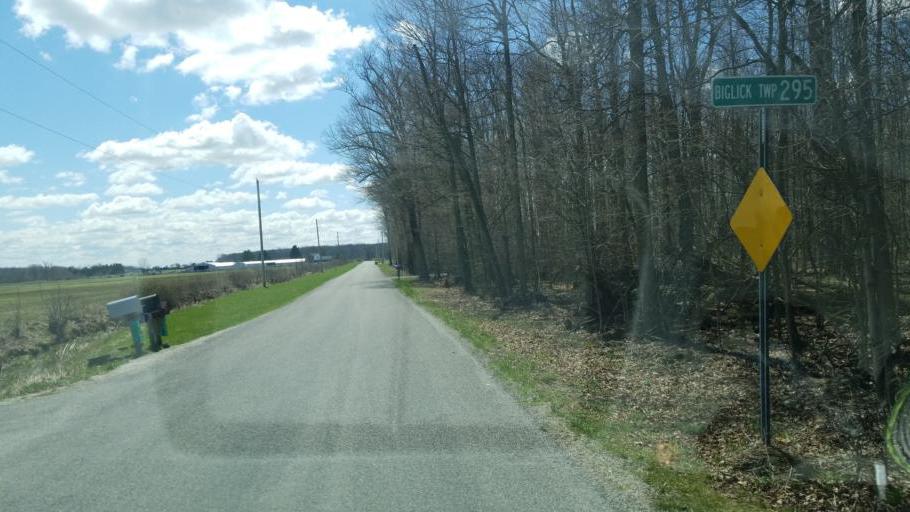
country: US
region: Ohio
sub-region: Hancock County
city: Findlay
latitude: 41.0430
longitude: -83.5153
